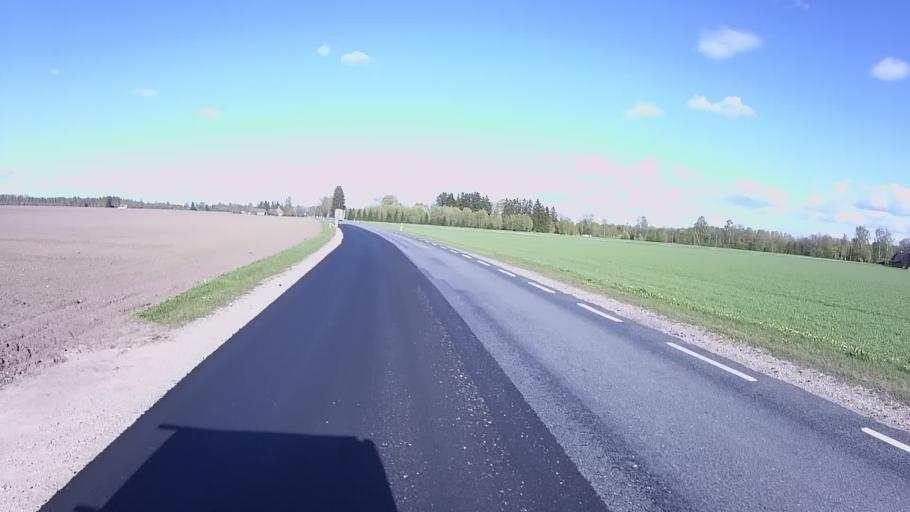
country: EE
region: Viljandimaa
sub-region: Vohma linn
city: Vohma
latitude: 58.6377
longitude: 25.6613
